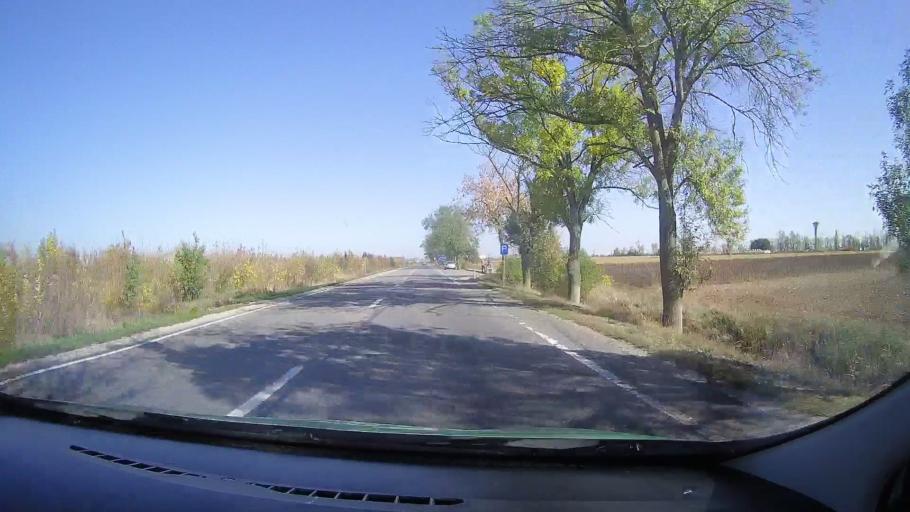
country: RO
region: Satu Mare
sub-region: Comuna Moftinu
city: Moftinu Mic
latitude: 47.7027
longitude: 22.6307
